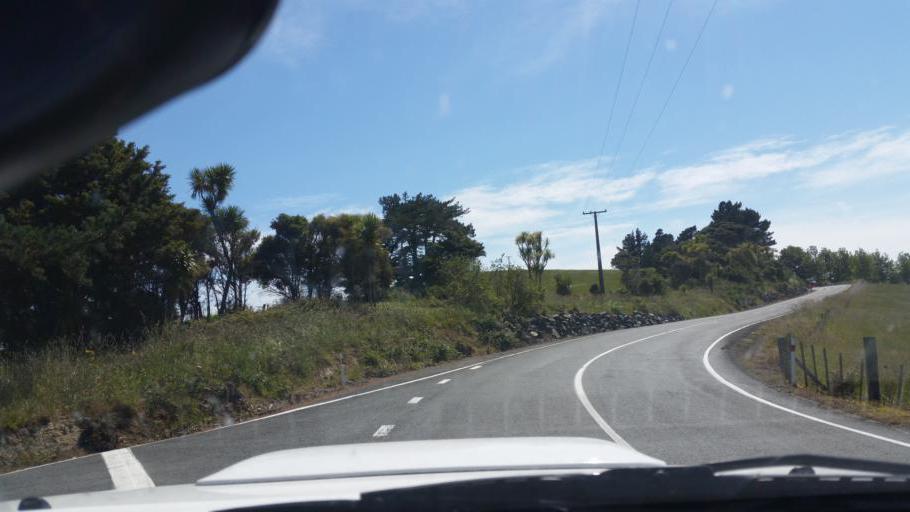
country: NZ
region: Auckland
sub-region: Auckland
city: Wellsford
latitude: -36.2242
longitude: 174.3752
